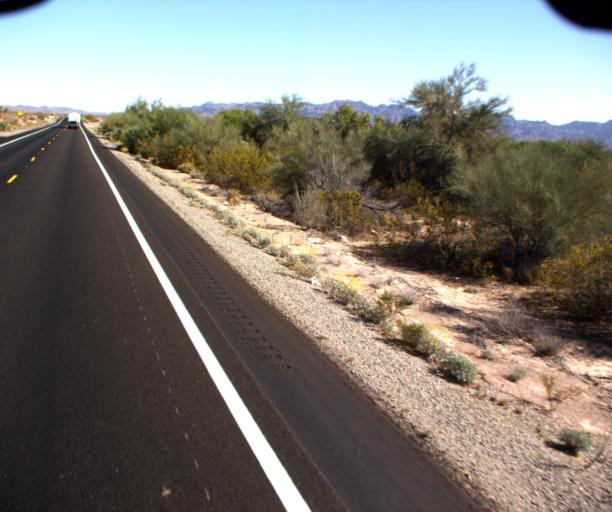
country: US
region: Arizona
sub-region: Yuma County
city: Wellton
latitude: 33.1092
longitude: -114.2957
